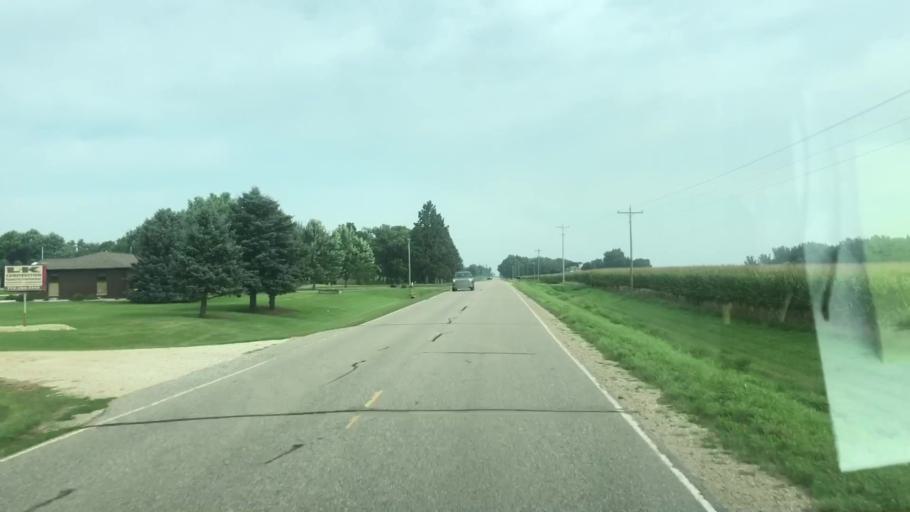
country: US
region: Iowa
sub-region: O'Brien County
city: Sheldon
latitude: 43.1946
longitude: -95.8622
